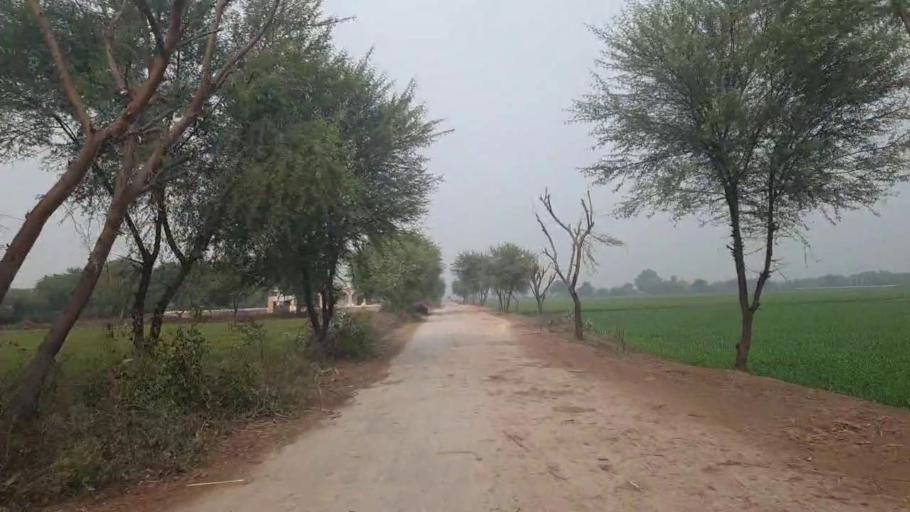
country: PK
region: Sindh
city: Tando Adam
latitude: 25.7671
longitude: 68.7025
